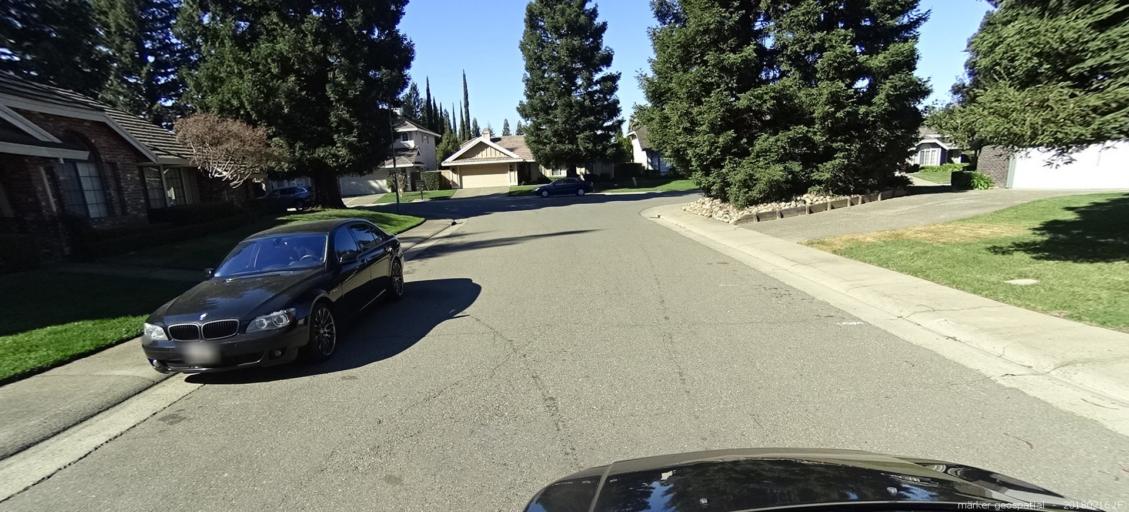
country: US
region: California
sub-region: Sacramento County
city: Gold River
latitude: 38.6213
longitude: -121.2559
